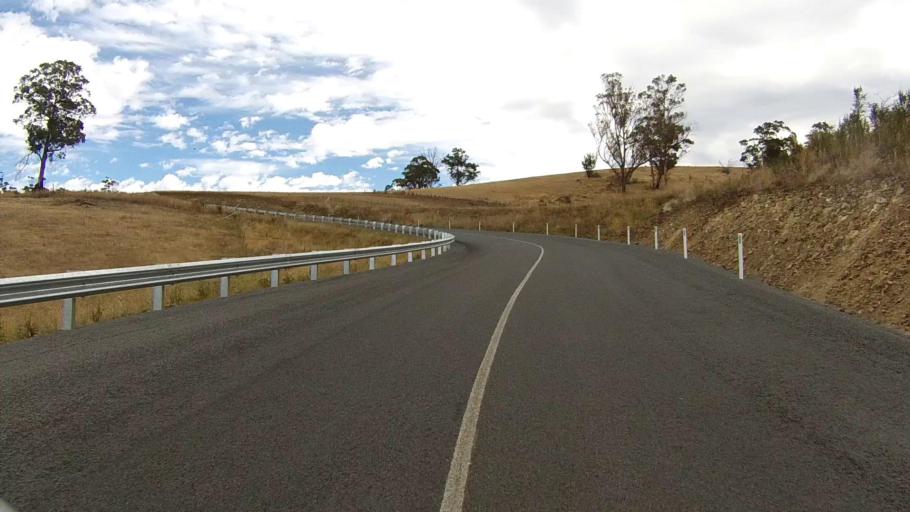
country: AU
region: Tasmania
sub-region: Sorell
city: Sorell
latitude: -42.8817
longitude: 147.7175
